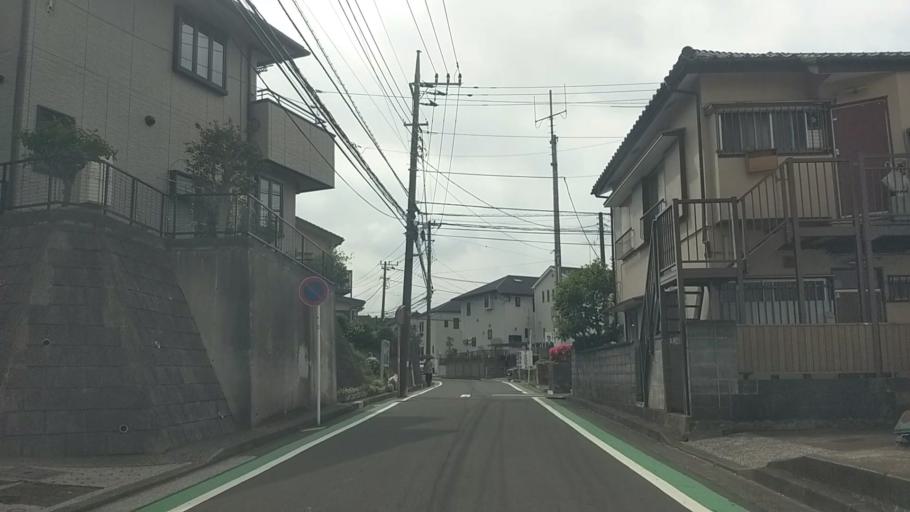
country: JP
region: Kanagawa
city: Kamakura
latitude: 35.3778
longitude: 139.5366
